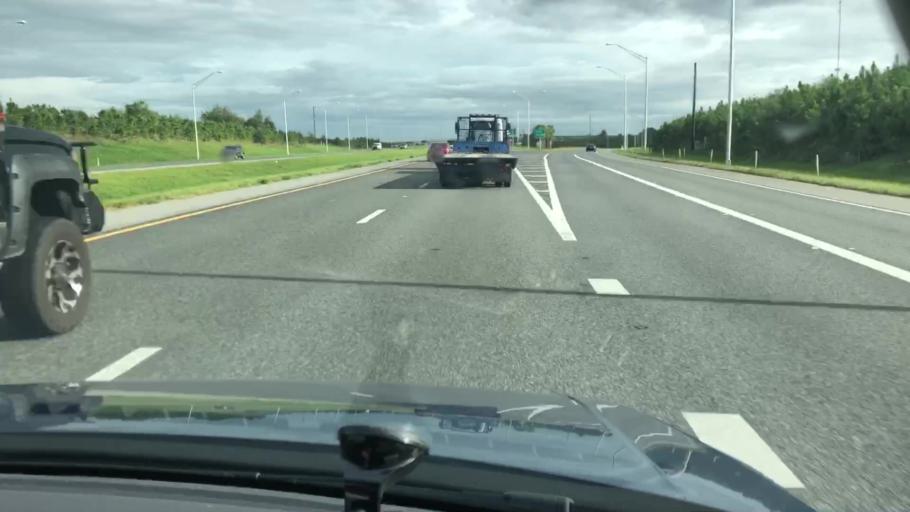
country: US
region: Florida
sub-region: Orange County
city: Paradise Heights
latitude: 28.6575
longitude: -81.5495
